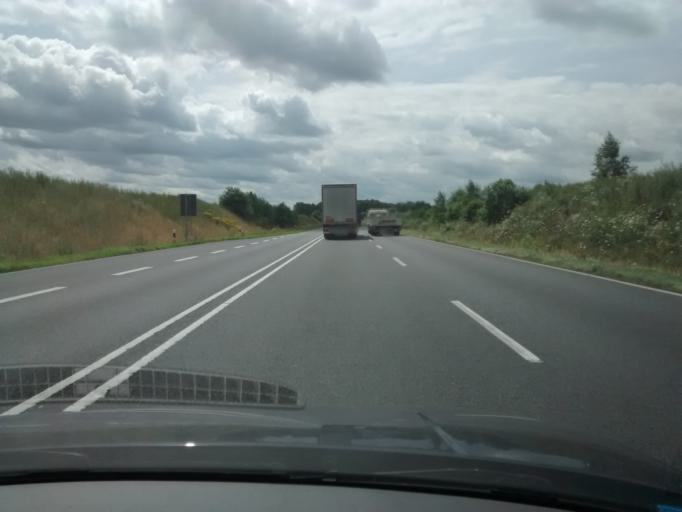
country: DE
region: Lower Saxony
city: Lastrup
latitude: 52.8003
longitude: 7.8487
